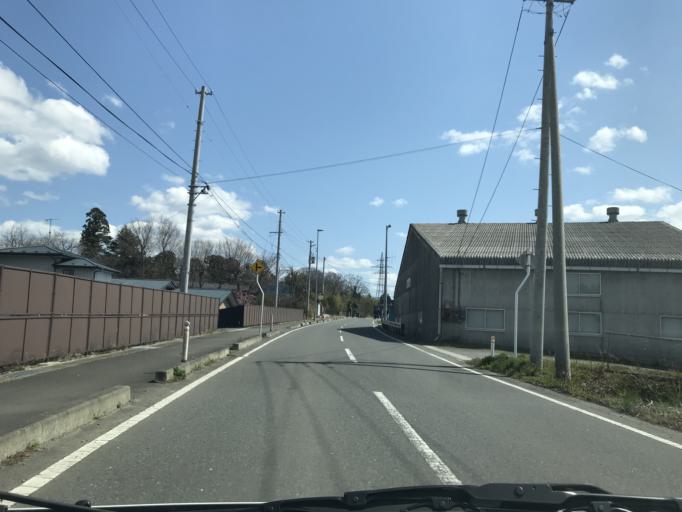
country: JP
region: Miyagi
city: Wakuya
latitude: 38.6274
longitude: 141.2251
